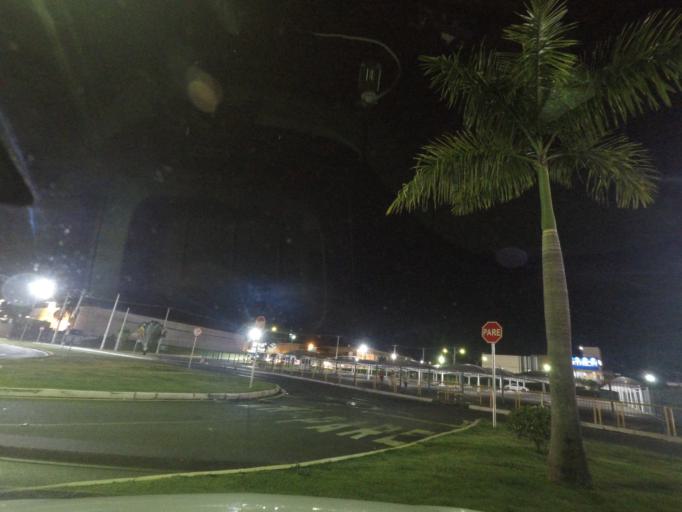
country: BR
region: Goias
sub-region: Goiania
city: Goiania
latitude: -16.7121
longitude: -49.2362
